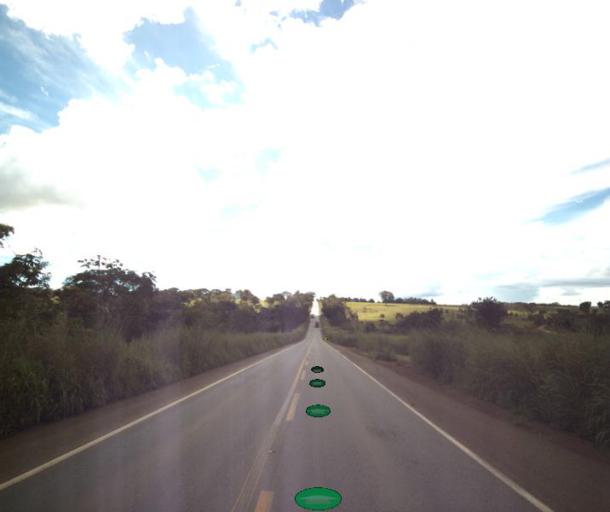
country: BR
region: Goias
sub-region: Jaragua
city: Jaragua
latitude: -15.8669
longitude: -49.2565
